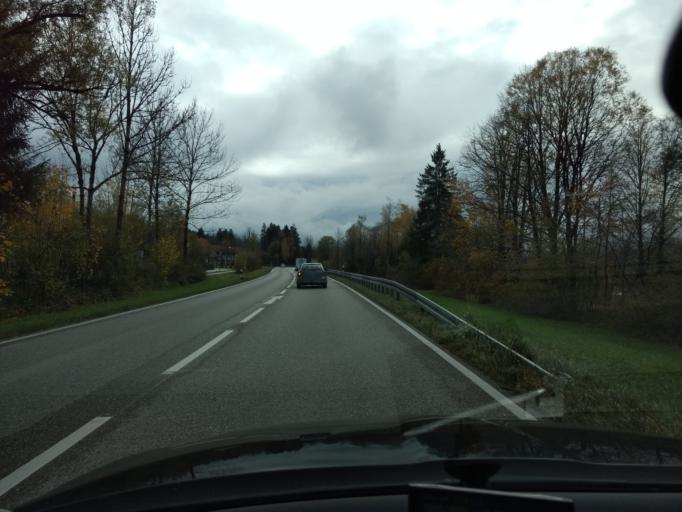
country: DE
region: Bavaria
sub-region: Upper Bavaria
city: Lenggries
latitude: 47.6738
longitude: 11.5728
